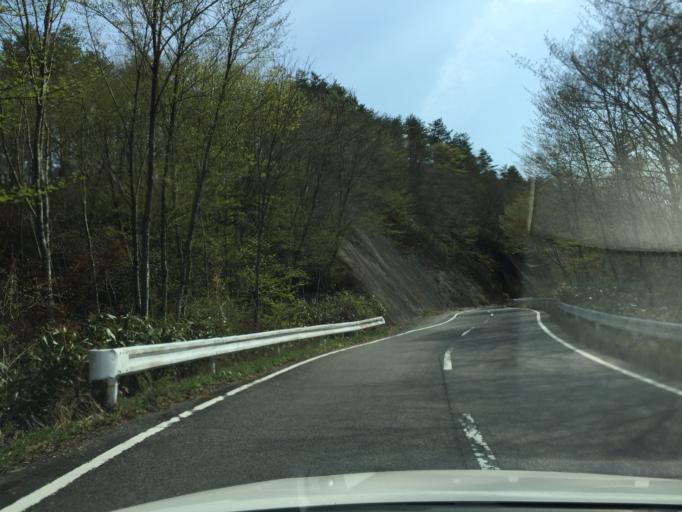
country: JP
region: Fukushima
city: Iwaki
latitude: 37.2279
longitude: 140.8447
